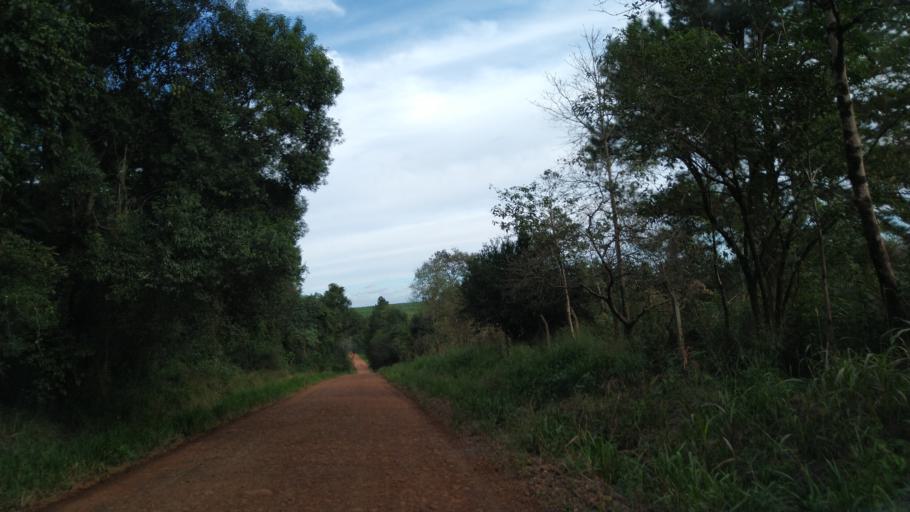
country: AR
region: Misiones
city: Capiovi
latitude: -26.9346
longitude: -55.0967
